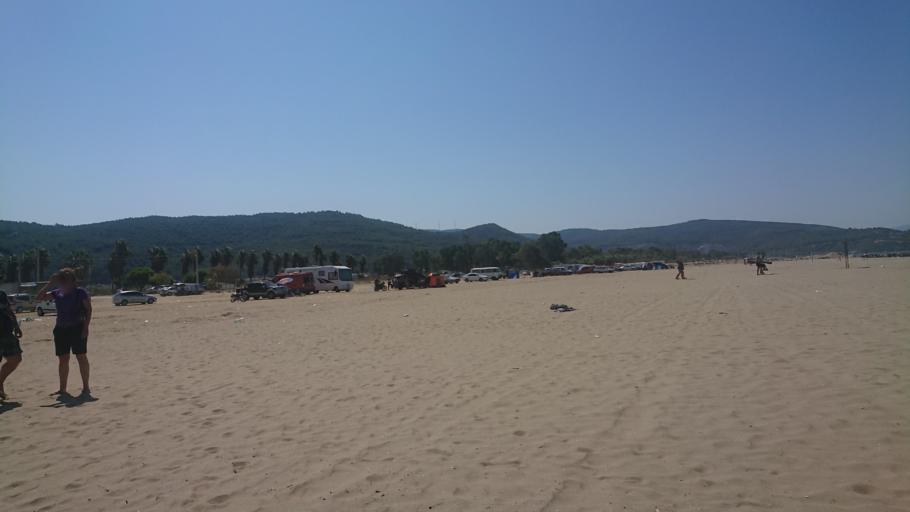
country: TR
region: Aydin
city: Kusadasi
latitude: 37.9440
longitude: 27.2734
